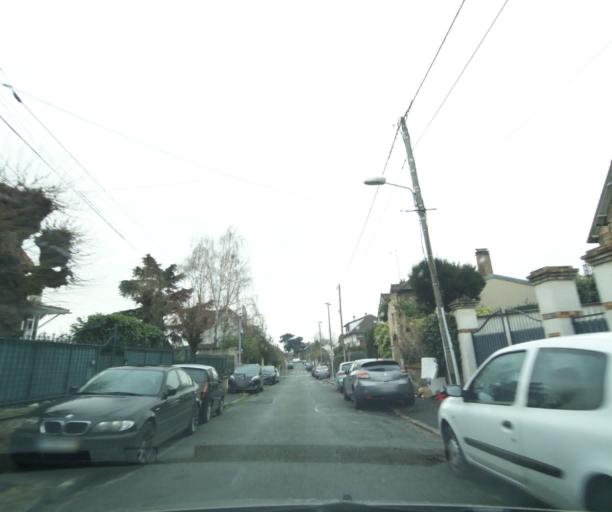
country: FR
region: Ile-de-France
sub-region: Departement du Val-de-Marne
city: Ablon-sur-Seine
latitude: 48.7332
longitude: 2.4166
